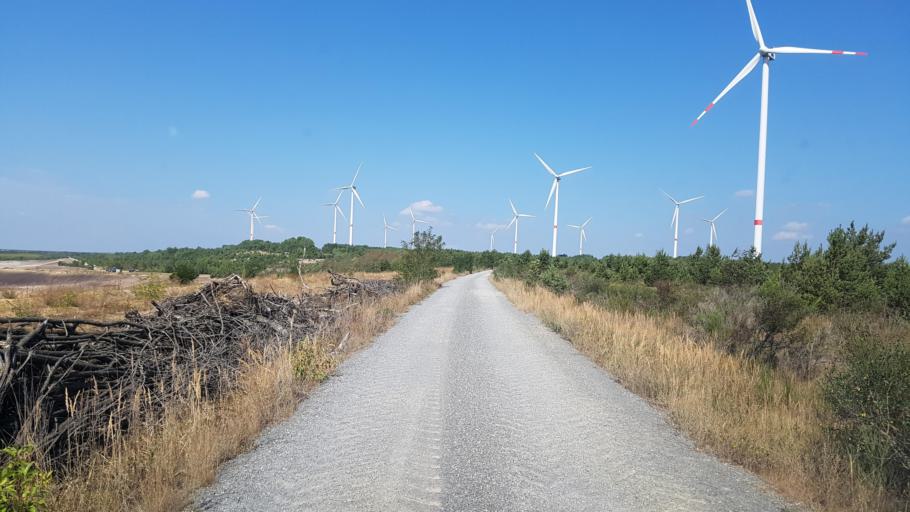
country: DE
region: Brandenburg
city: Sallgast
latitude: 51.5476
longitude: 13.8488
